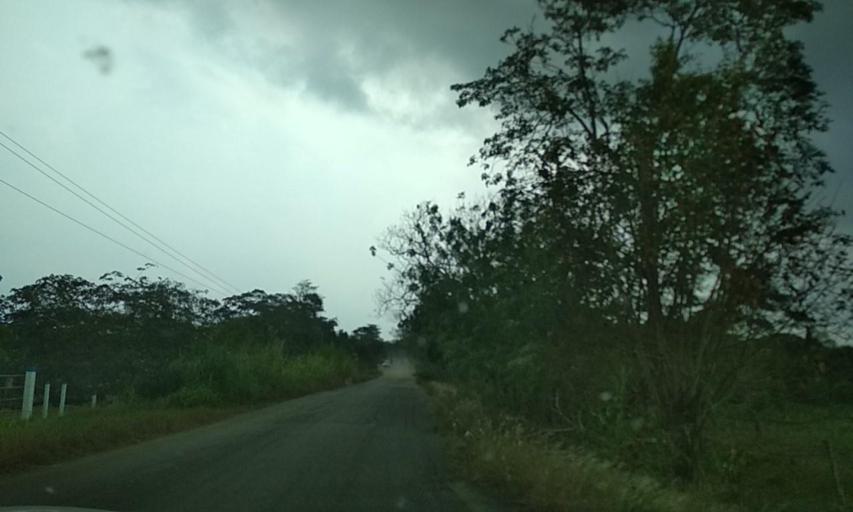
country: MX
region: Tabasco
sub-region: Huimanguillo
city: Francisco Rueda
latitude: 17.5628
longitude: -94.1158
